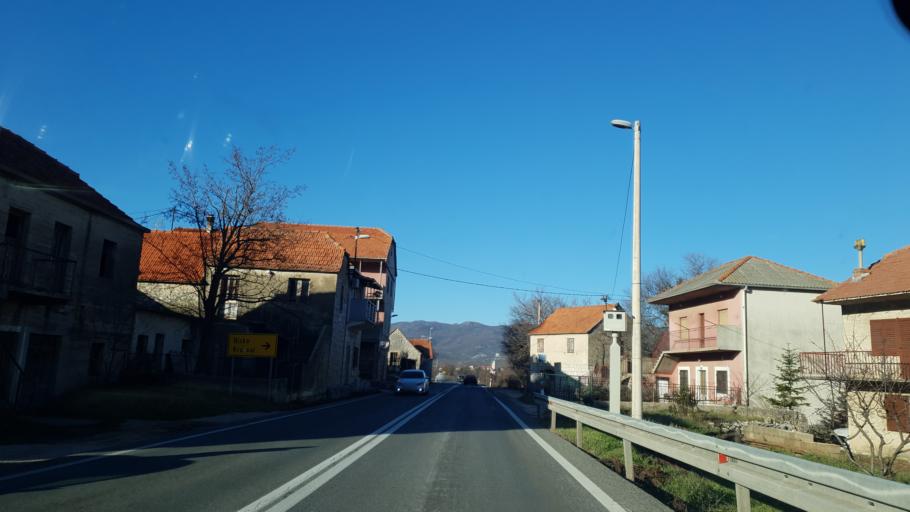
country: HR
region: Splitsko-Dalmatinska
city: Dugopolje
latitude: 43.6164
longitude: 16.5974
